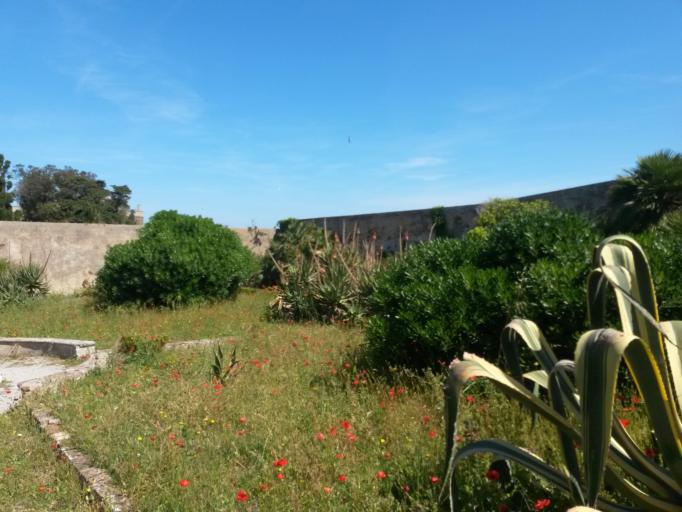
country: IT
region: Tuscany
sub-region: Provincia di Livorno
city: Portoferraio
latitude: 42.8164
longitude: 10.3328
